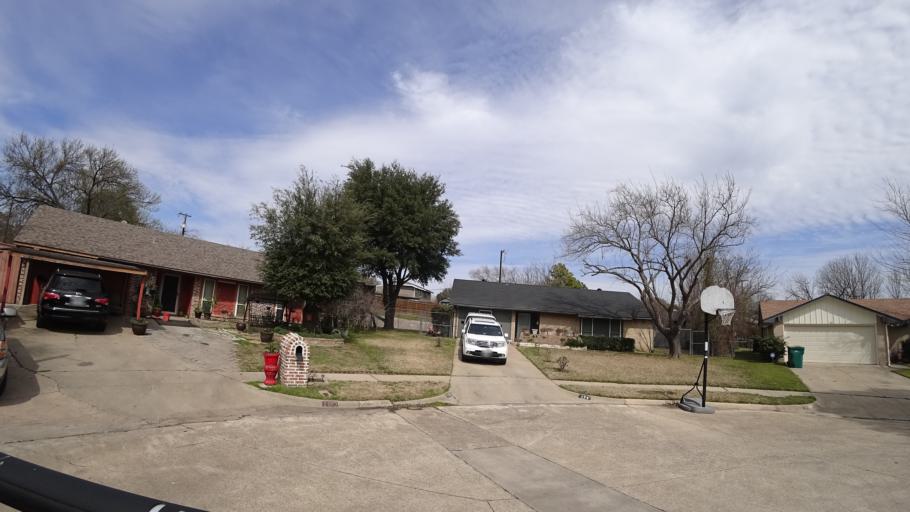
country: US
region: Texas
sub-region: Denton County
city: Lewisville
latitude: 33.0398
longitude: -97.0129
